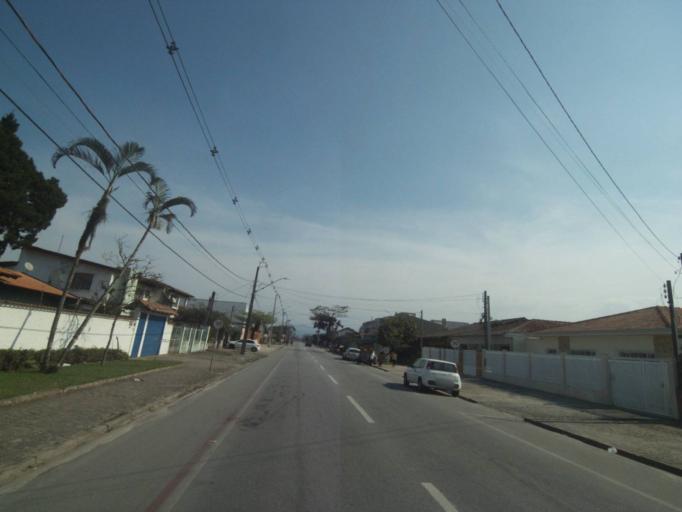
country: BR
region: Parana
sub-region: Paranagua
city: Paranagua
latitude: -25.5250
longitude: -48.5176
